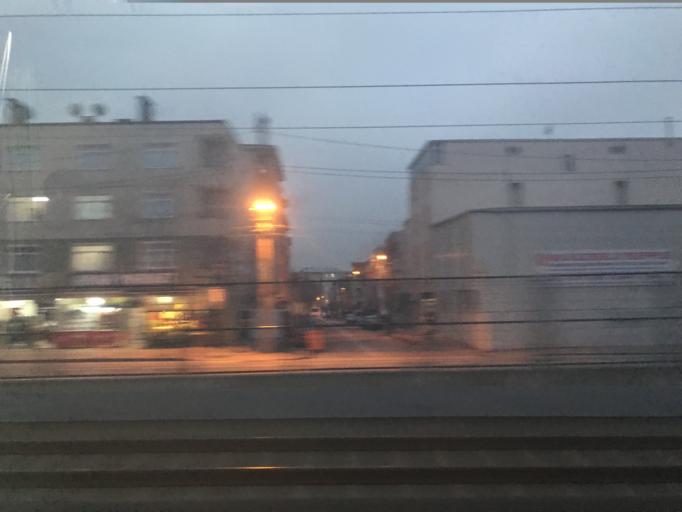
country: TR
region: Kocaeli
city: Darica
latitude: 40.7854
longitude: 29.4055
